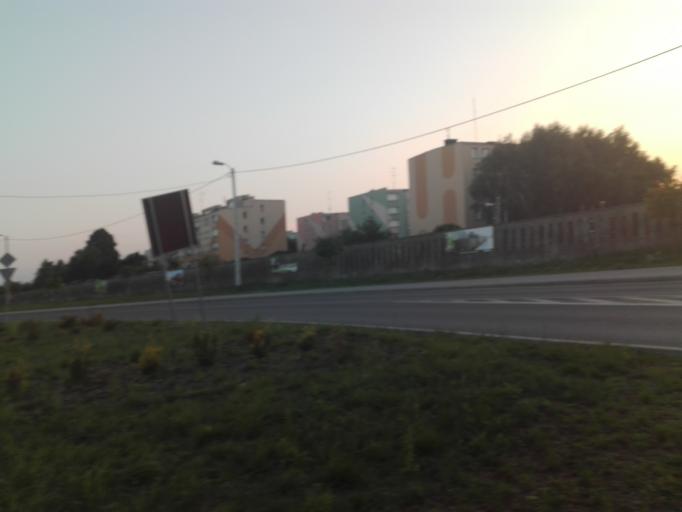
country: PL
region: Masovian Voivodeship
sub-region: Powiat sochaczewski
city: Sochaczew
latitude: 52.2197
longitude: 20.2394
